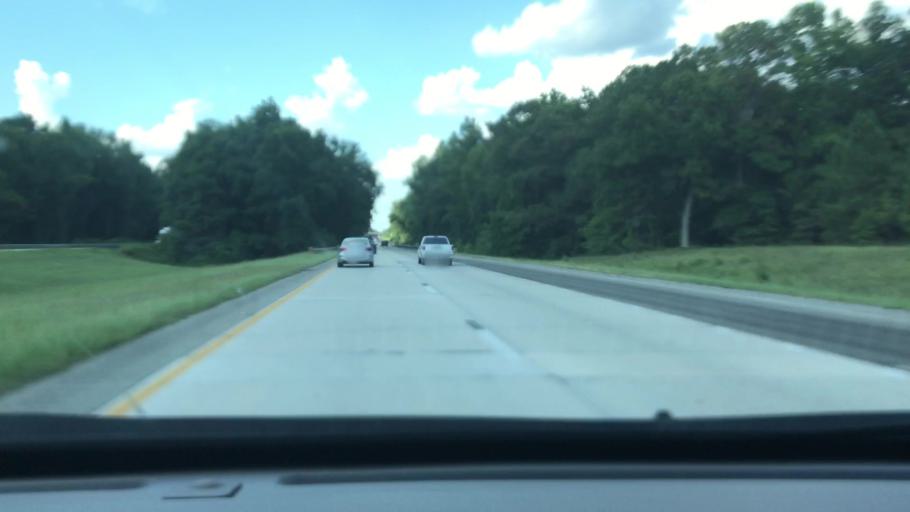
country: US
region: South Carolina
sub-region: Florence County
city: Timmonsville
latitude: 34.1150
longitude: -79.9067
